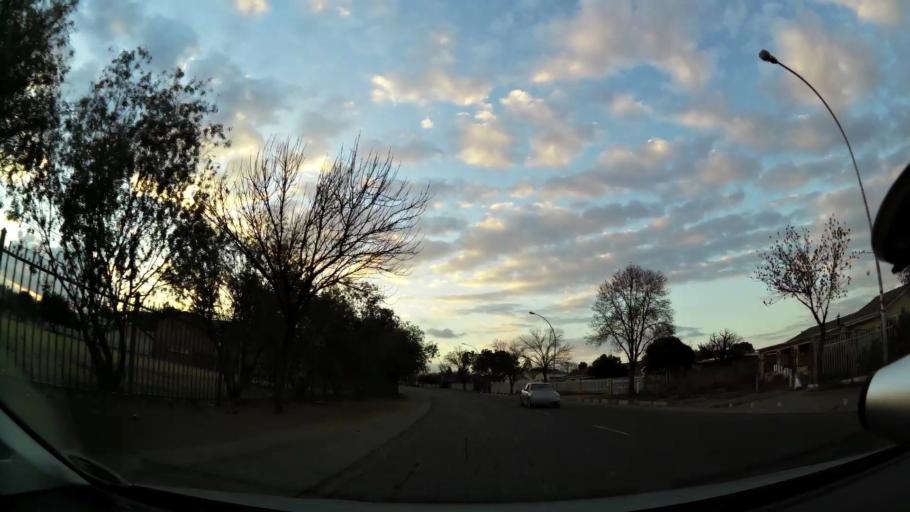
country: ZA
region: Orange Free State
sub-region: Mangaung Metropolitan Municipality
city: Bloemfontein
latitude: -29.1698
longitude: 26.1921
